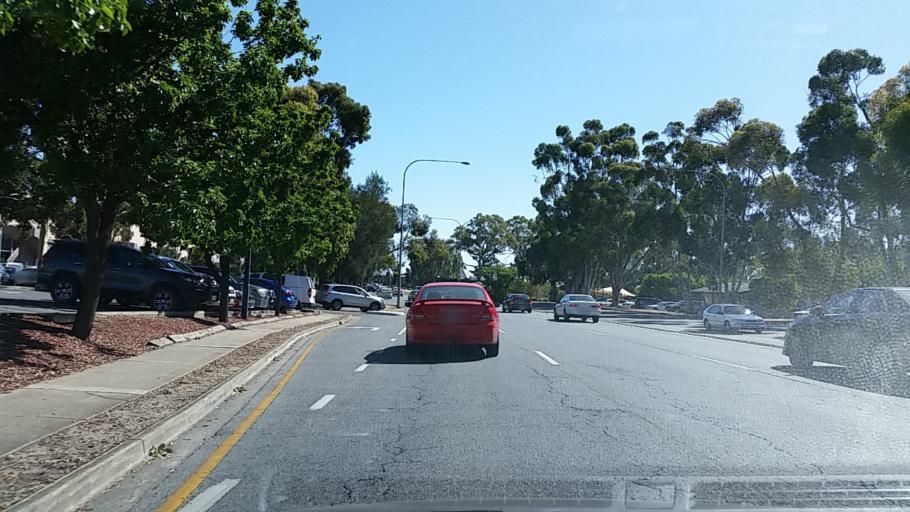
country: AU
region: South Australia
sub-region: Tea Tree Gully
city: Modbury
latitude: -34.8291
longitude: 138.6911
